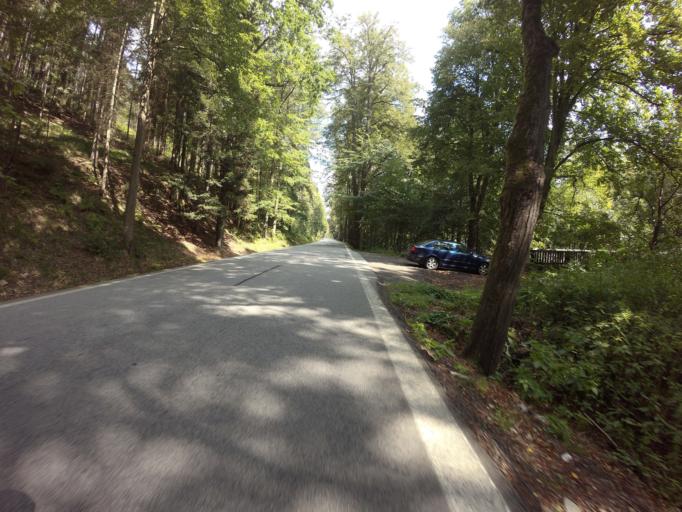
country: CZ
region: Jihocesky
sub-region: Okres Cesky Krumlov
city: Vyssi Brod
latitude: 48.6583
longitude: 14.3637
